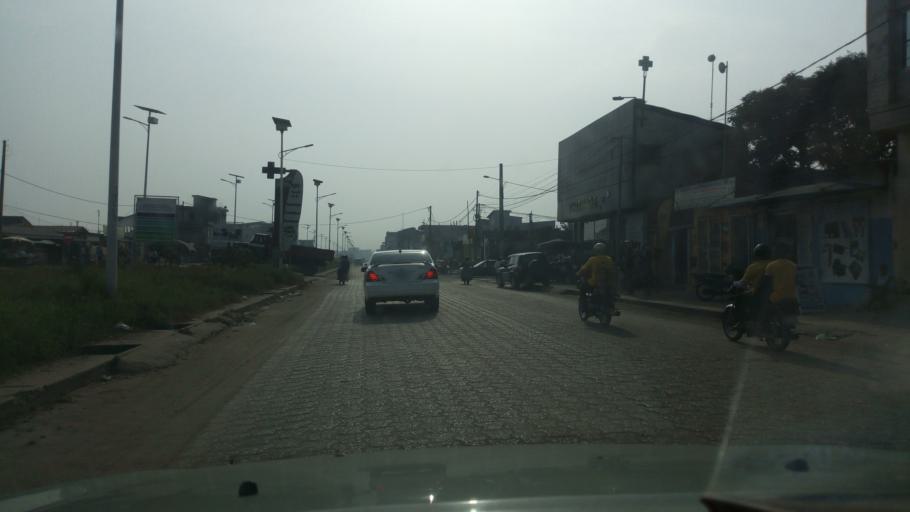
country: BJ
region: Littoral
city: Cotonou
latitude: 6.3749
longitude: 2.3502
